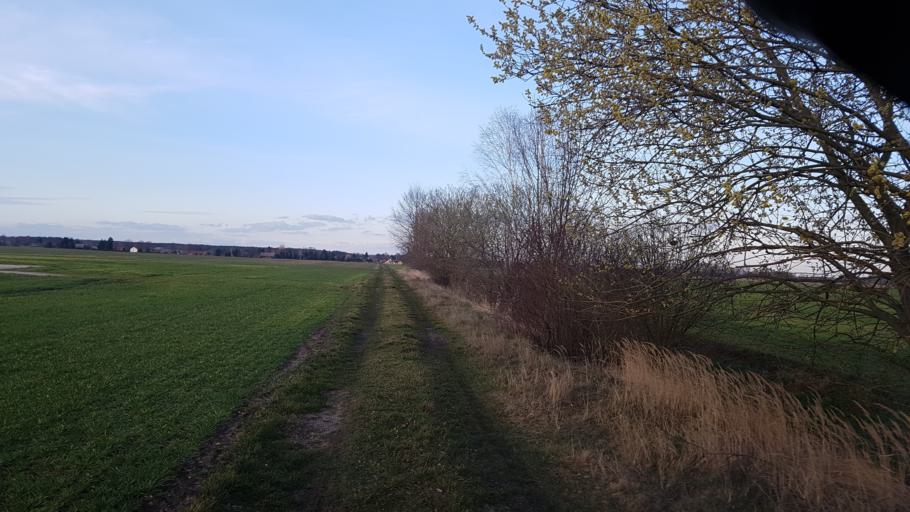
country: DE
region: Brandenburg
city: Schonborn
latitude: 51.5845
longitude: 13.5001
